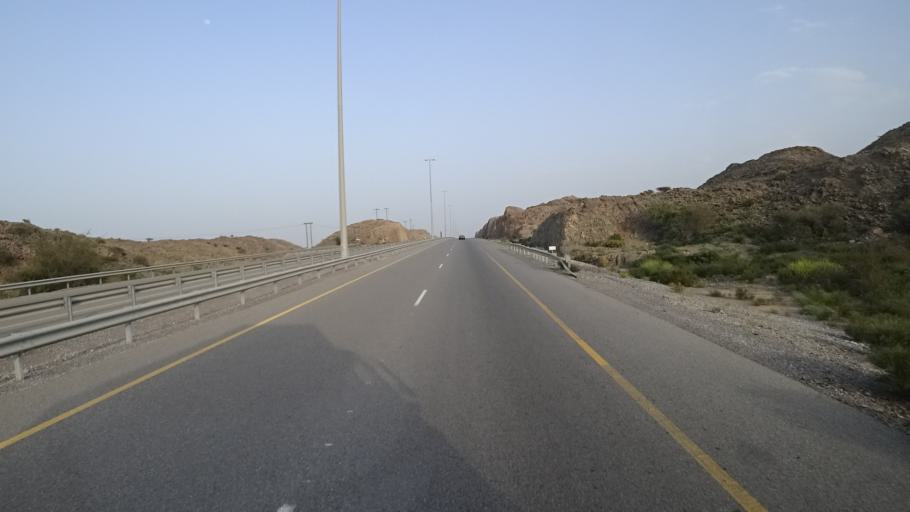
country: OM
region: Muhafazat Masqat
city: Muscat
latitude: 23.2054
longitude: 58.8138
